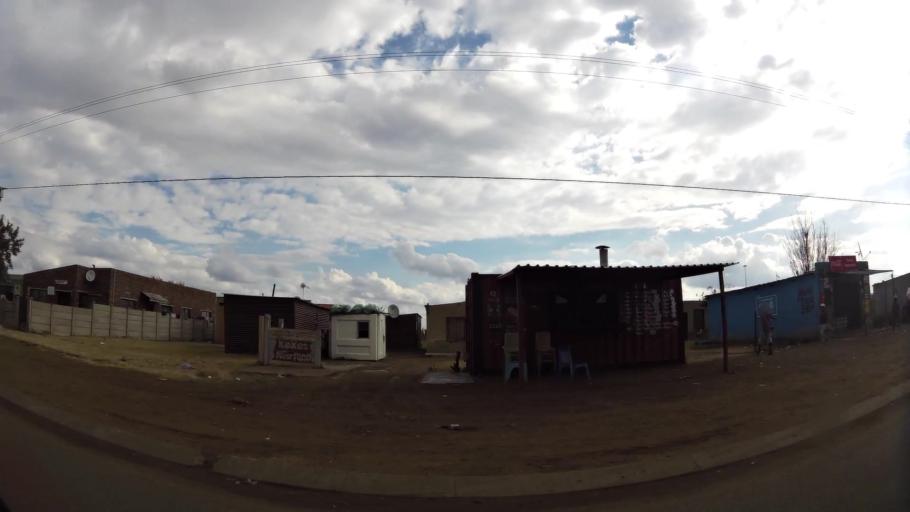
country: ZA
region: Gauteng
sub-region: Sedibeng District Municipality
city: Vanderbijlpark
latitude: -26.6942
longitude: 27.7838
